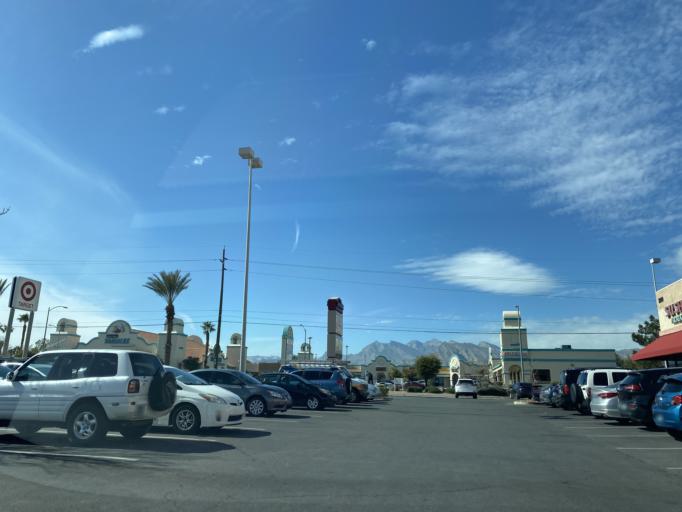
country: US
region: Nevada
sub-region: Clark County
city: Spring Valley
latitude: 36.2197
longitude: -115.2506
